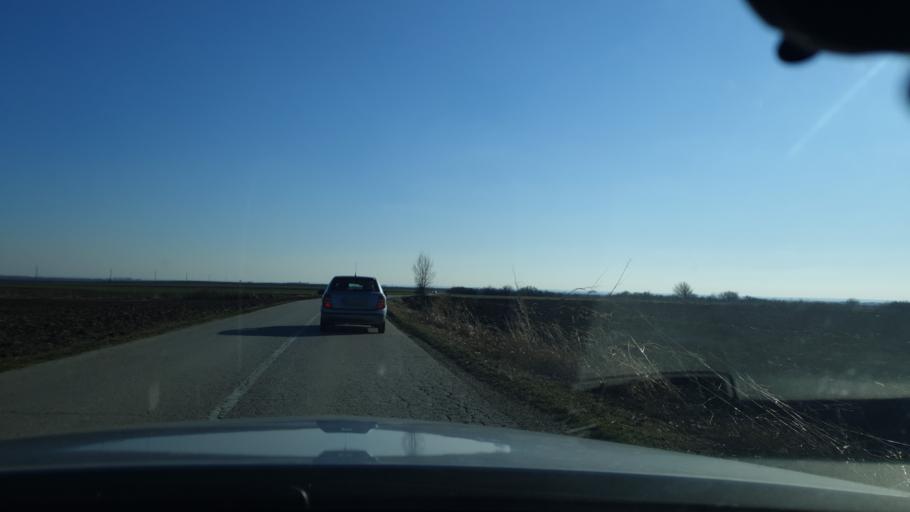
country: RS
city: Vrdnik
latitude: 45.0726
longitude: 19.8091
